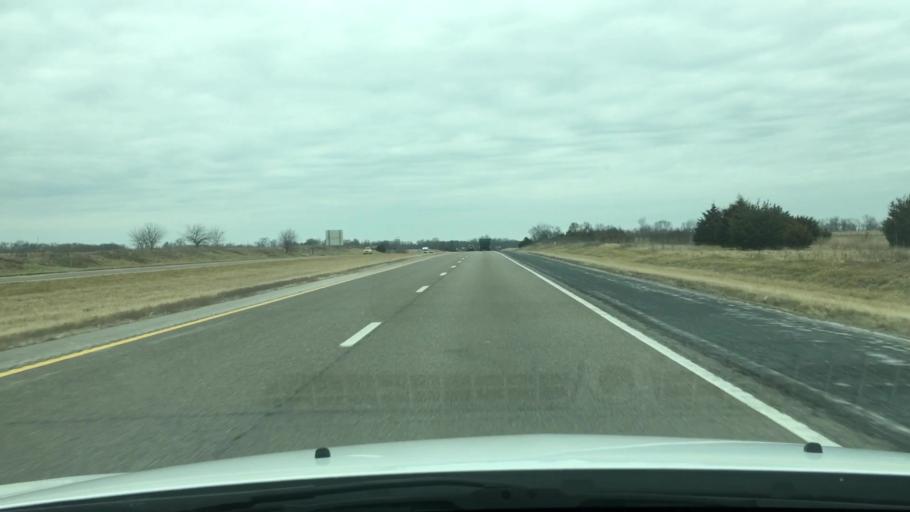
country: US
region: Missouri
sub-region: Audrain County
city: Mexico
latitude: 39.0333
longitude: -91.8880
